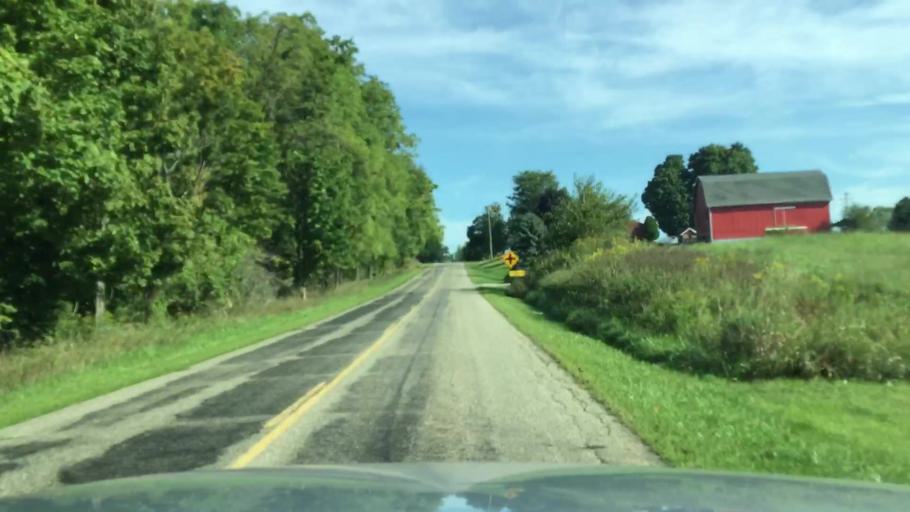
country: US
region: Michigan
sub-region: Lenawee County
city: Hudson
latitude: 41.9256
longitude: -84.4205
